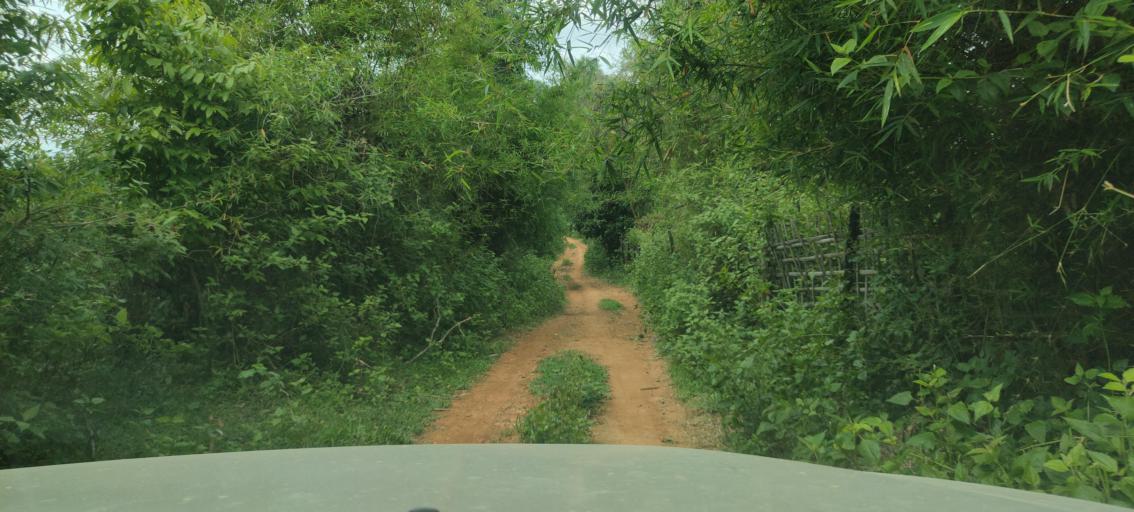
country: LA
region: Loungnamtha
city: Muang Nale
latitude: 20.4303
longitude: 101.4718
